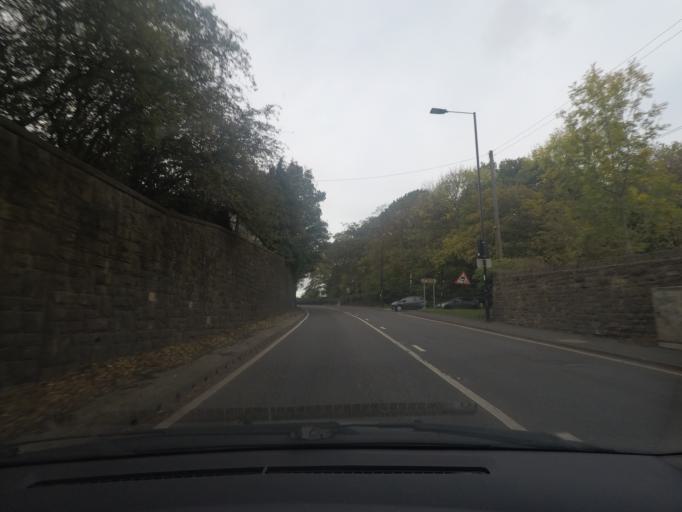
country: GB
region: England
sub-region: Sheffield
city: Chapletown
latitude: 53.4551
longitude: -1.4945
